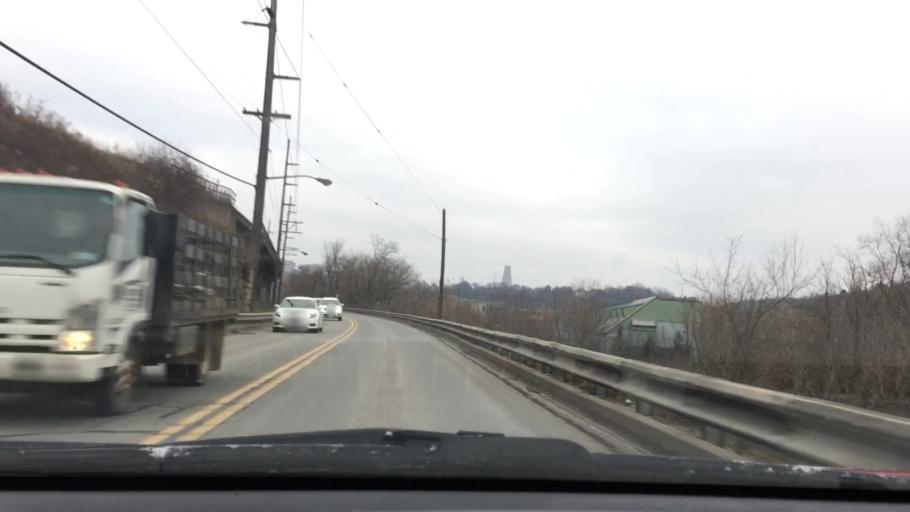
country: US
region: Pennsylvania
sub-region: Allegheny County
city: Mount Oliver
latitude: 40.4147
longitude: -79.9557
